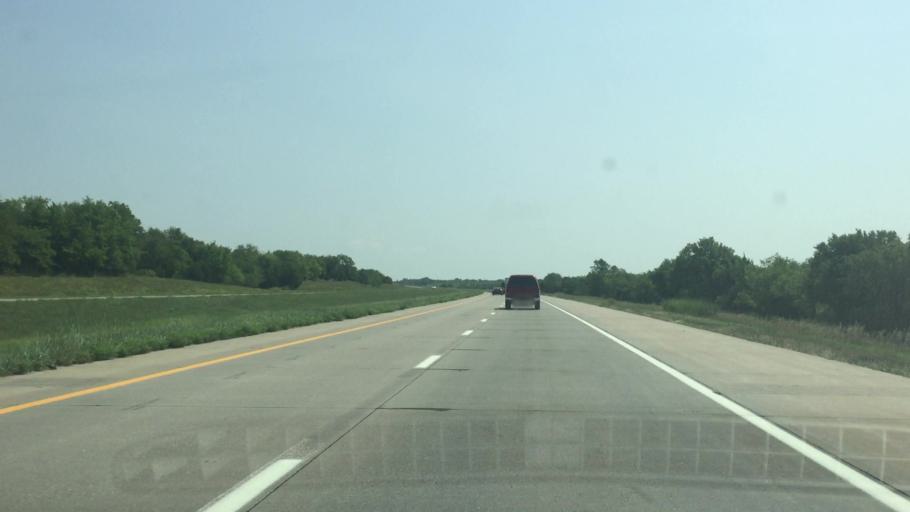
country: US
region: Kansas
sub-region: Osage County
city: Lyndon
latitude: 38.4527
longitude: -95.5799
